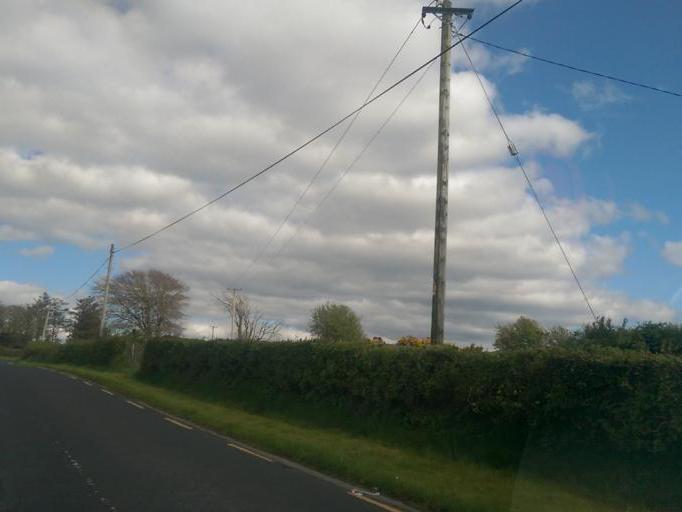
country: IE
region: Connaught
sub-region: County Galway
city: Ballinasloe
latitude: 53.4322
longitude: -8.4563
